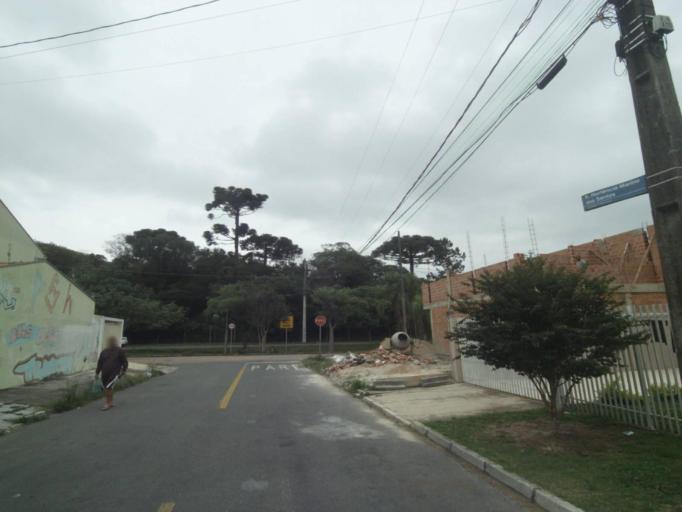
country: BR
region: Parana
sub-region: Araucaria
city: Araucaria
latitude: -25.5398
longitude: -49.3396
